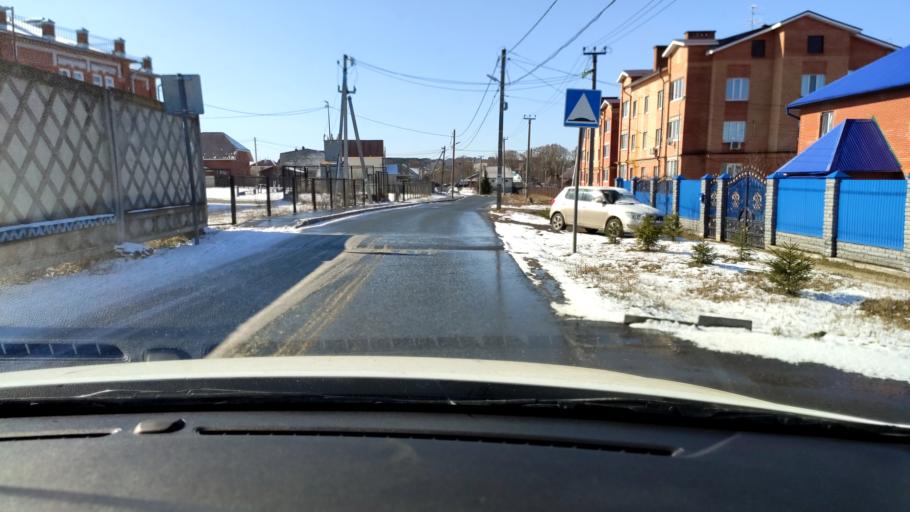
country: RU
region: Tatarstan
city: Vysokaya Gora
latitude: 55.8743
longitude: 49.2453
